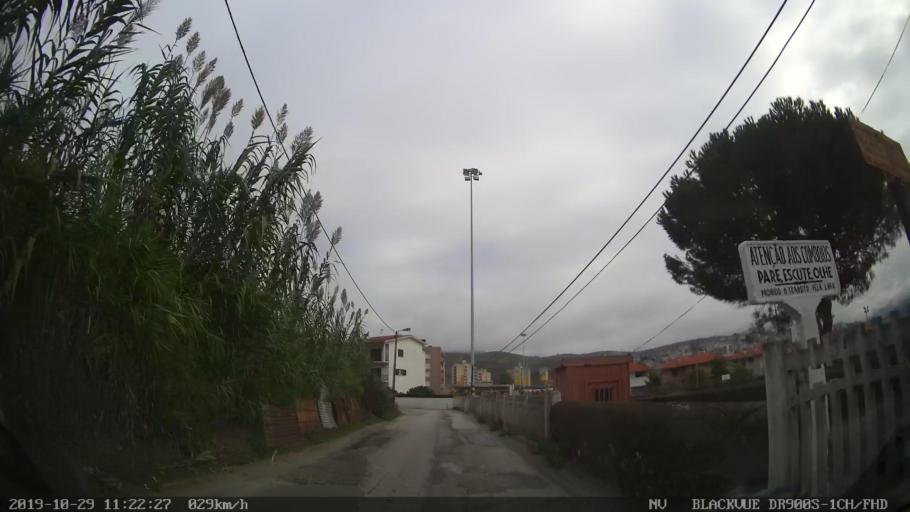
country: PT
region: Vila Real
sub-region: Peso da Regua
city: Godim
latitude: 41.1652
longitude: -7.8024
